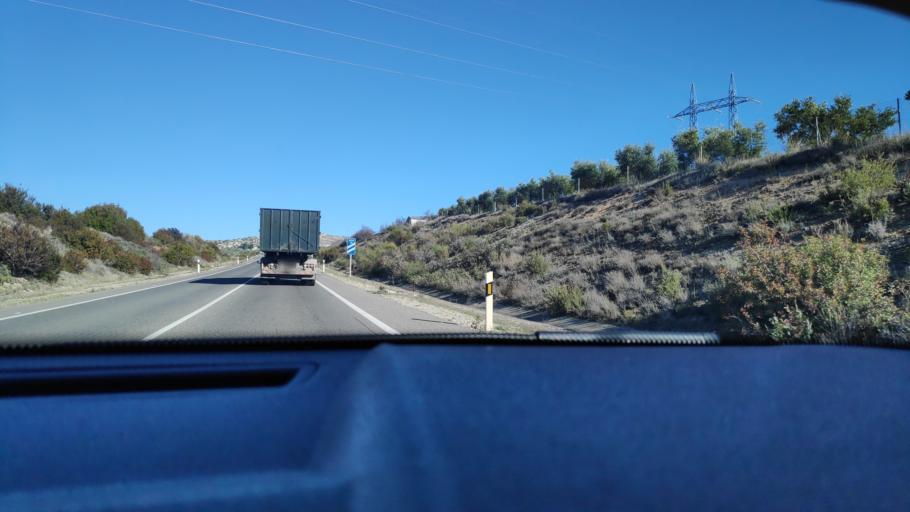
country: ES
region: Andalusia
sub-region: Province of Cordoba
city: Baena
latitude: 37.6174
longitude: -4.3007
